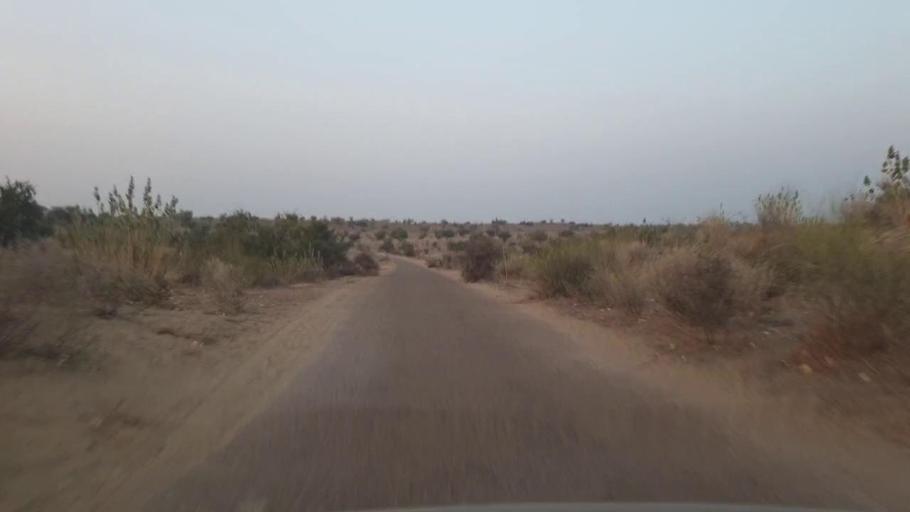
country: PK
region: Sindh
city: Umarkot
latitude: 25.3339
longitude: 70.0578
